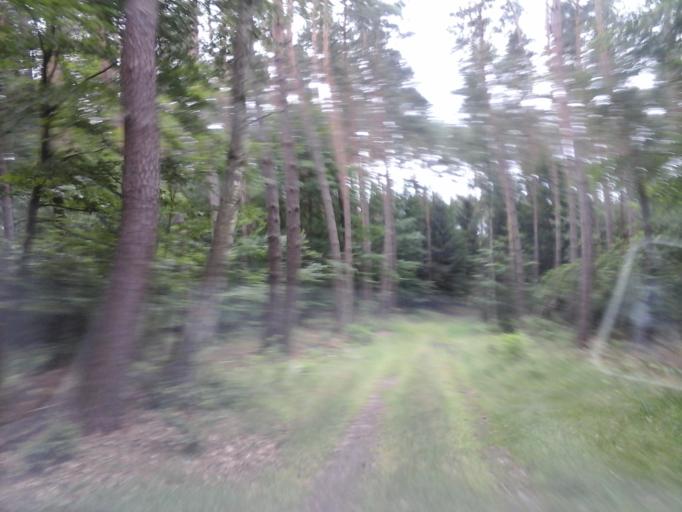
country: PL
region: West Pomeranian Voivodeship
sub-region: Powiat choszczenski
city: Pelczyce
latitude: 52.9591
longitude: 15.3552
